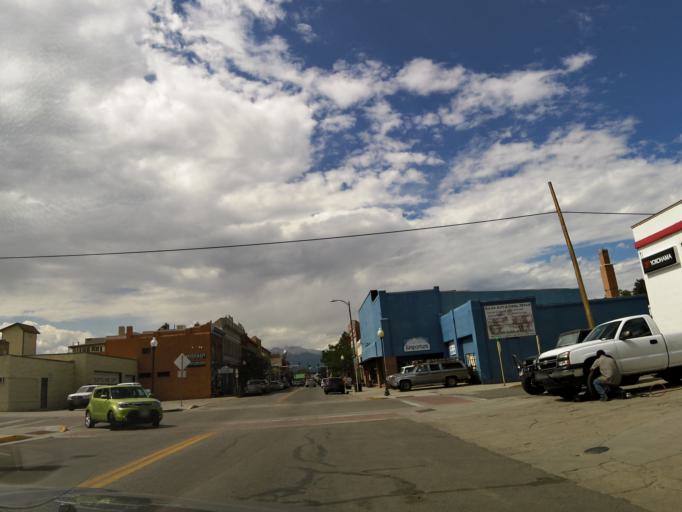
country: US
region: Colorado
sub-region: Chaffee County
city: Salida
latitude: 38.5355
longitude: -105.9904
